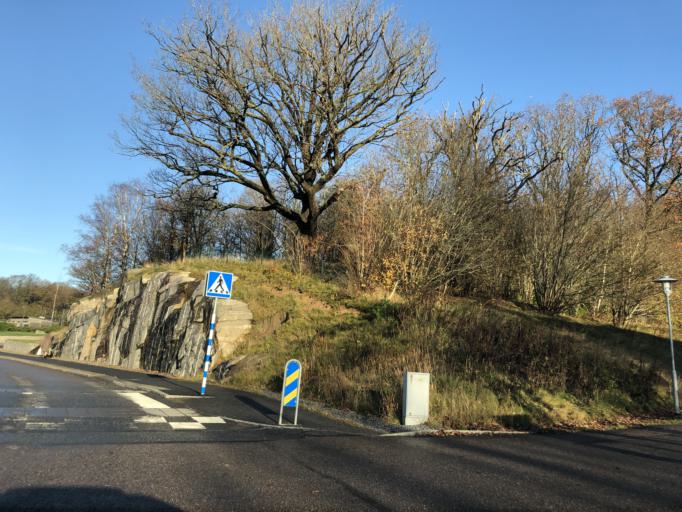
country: SE
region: Vaestra Goetaland
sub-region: Goteborg
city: Loevgaerdet
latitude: 57.7989
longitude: 12.0489
